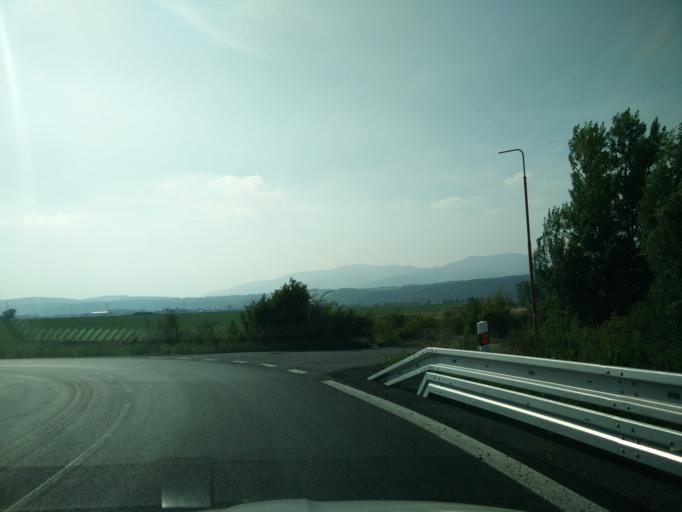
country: SK
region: Nitriansky
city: Novaky
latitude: 48.7251
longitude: 18.5739
